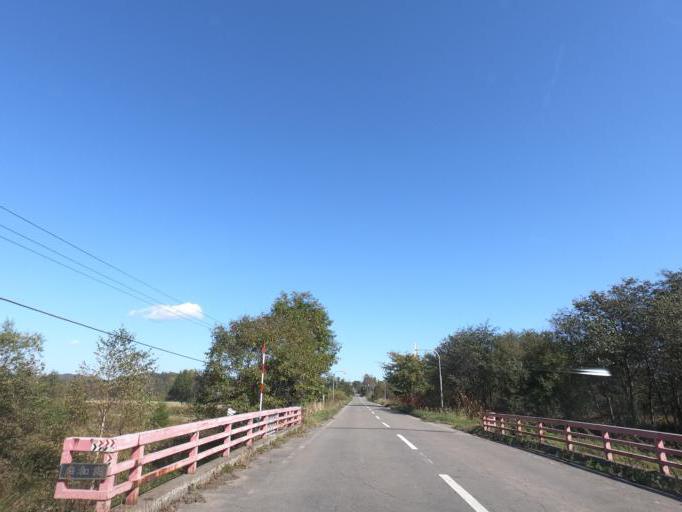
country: JP
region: Hokkaido
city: Obihiro
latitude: 42.6762
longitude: 143.3135
